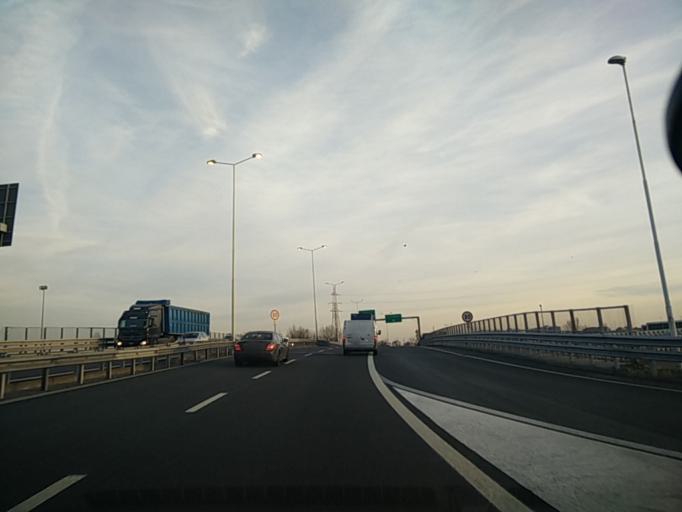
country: IT
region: Lombardy
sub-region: Provincia di Monza e Brianza
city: Monza
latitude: 45.5563
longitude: 9.2654
